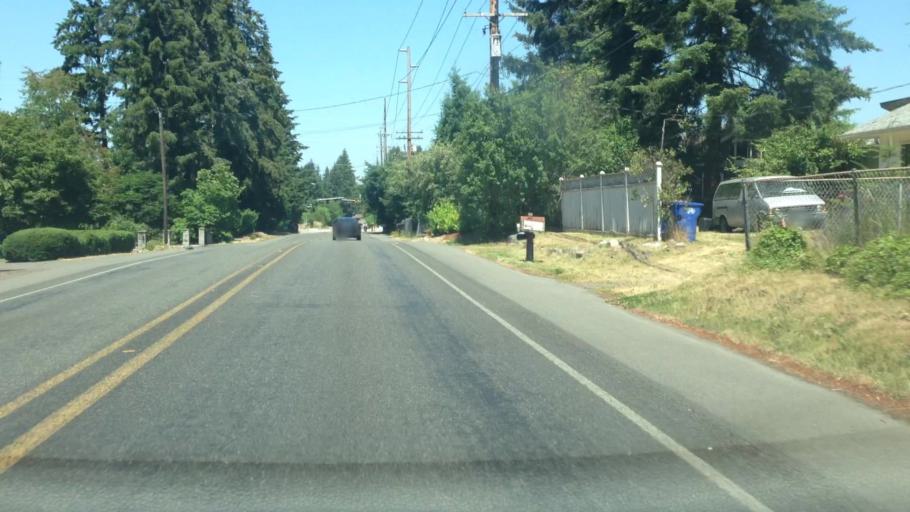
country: US
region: Washington
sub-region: Pierce County
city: Puyallup
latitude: 47.1530
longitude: -122.3148
